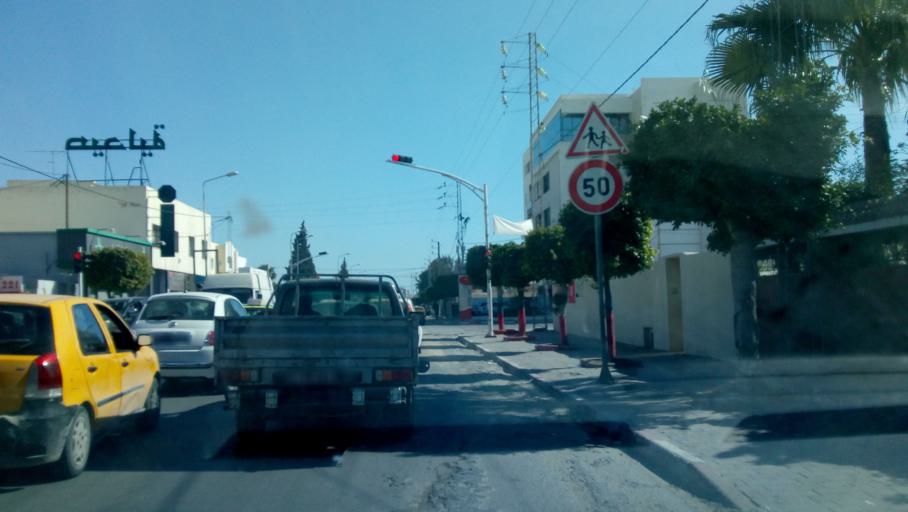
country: TN
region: Safaqis
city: Sfax
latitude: 34.7708
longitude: 10.7324
